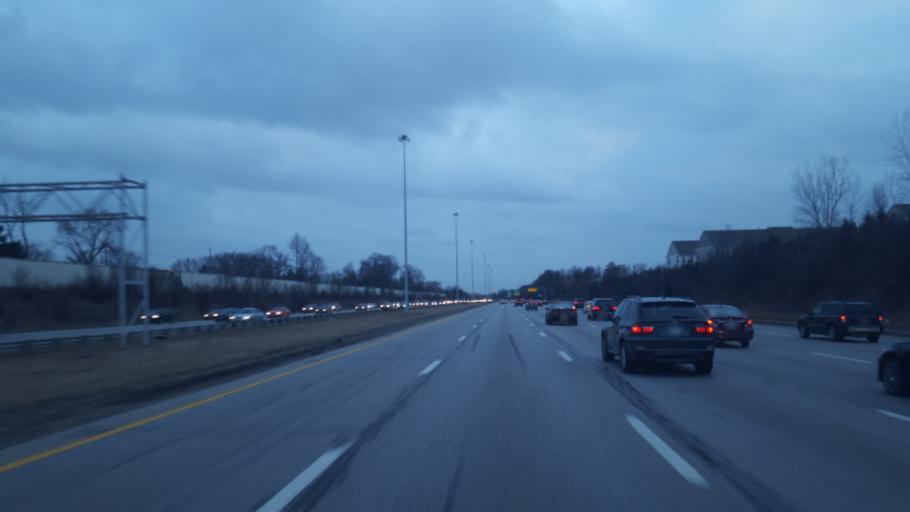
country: US
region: Ohio
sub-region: Franklin County
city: Gahanna
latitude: 40.0320
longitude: -82.9035
